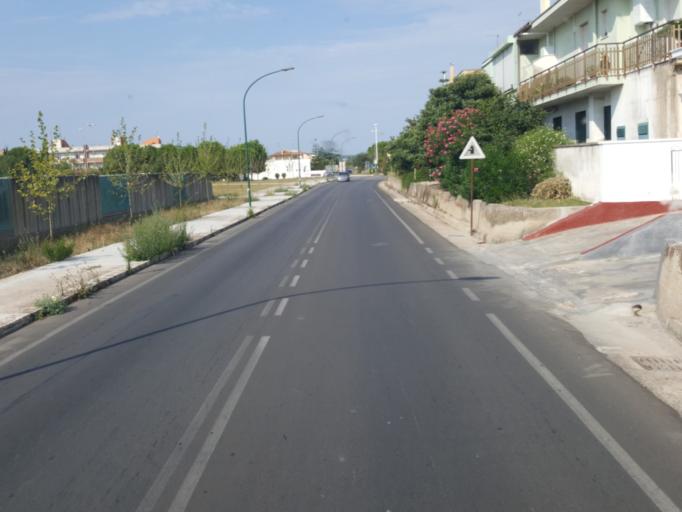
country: IT
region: Apulia
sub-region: Provincia di Lecce
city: Campi Salentina
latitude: 40.4021
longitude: 18.0142
